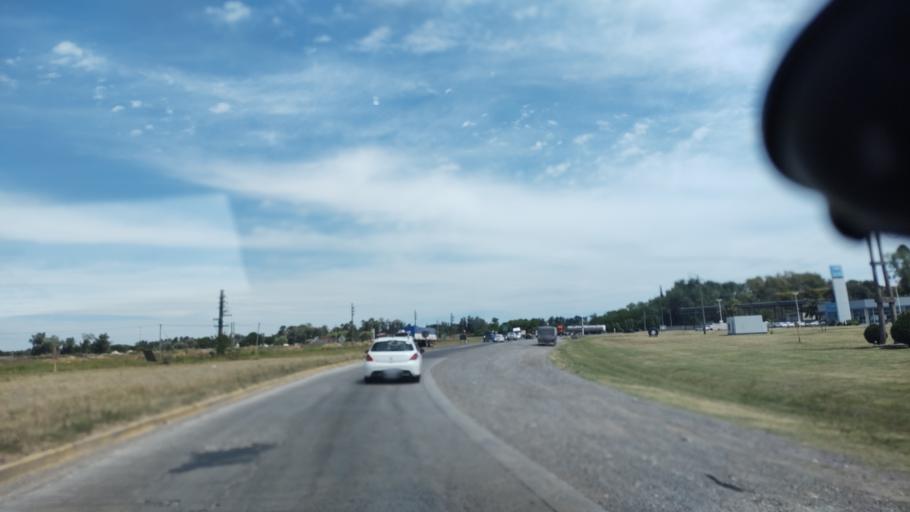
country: AR
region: Buenos Aires
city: Canuelas
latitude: -35.0204
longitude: -58.7476
